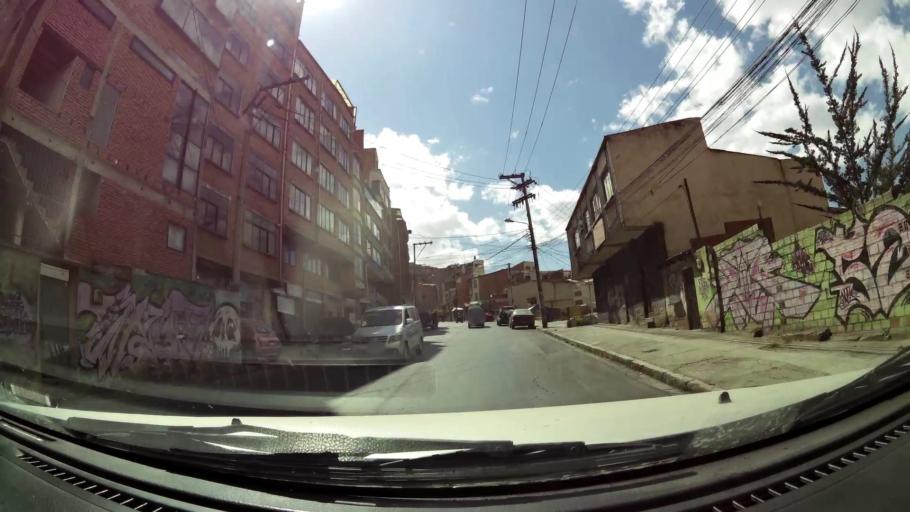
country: BO
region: La Paz
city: La Paz
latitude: -16.4907
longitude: -68.1253
